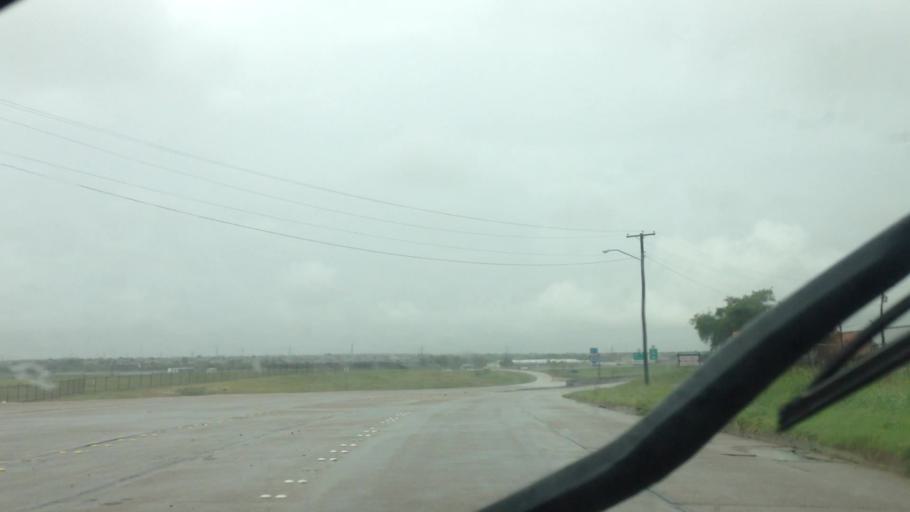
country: US
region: Texas
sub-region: Tarrant County
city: Saginaw
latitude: 32.8313
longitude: -97.3597
